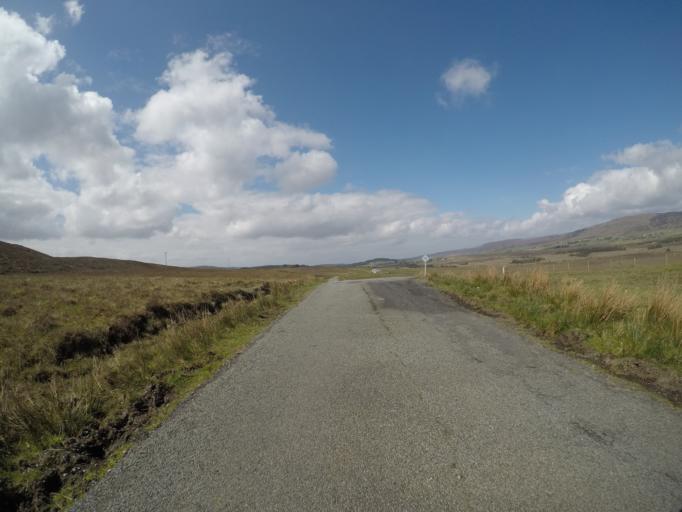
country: GB
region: Scotland
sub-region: Highland
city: Isle of Skye
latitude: 57.4278
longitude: -6.2717
